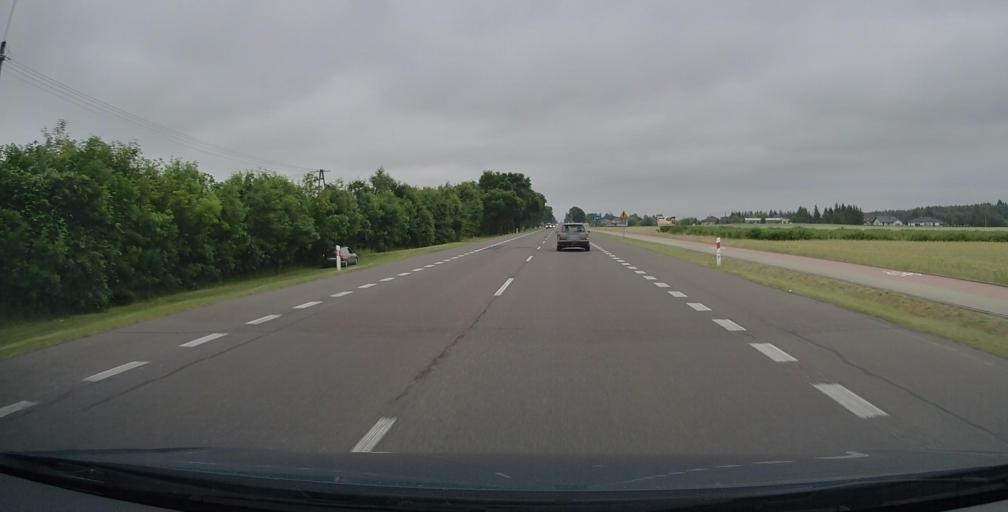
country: PL
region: Lublin Voivodeship
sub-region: Powiat bialski
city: Lesna Podlaska
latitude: 52.0359
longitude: 23.0117
